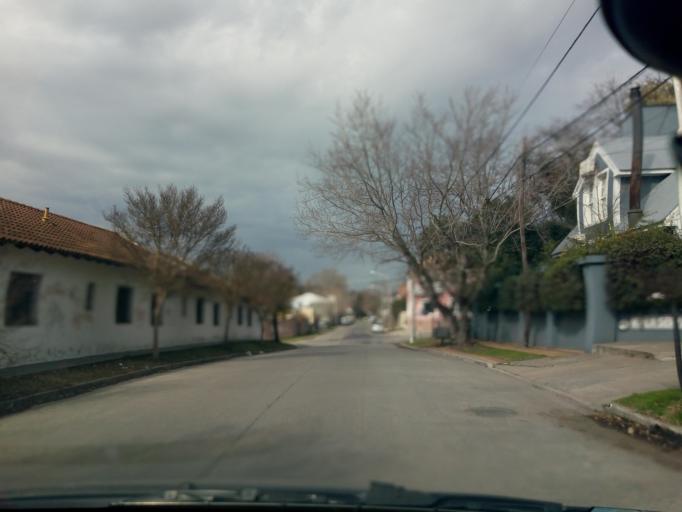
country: AR
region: Buenos Aires
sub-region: Partido de Tandil
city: Tandil
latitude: -37.3388
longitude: -59.1323
